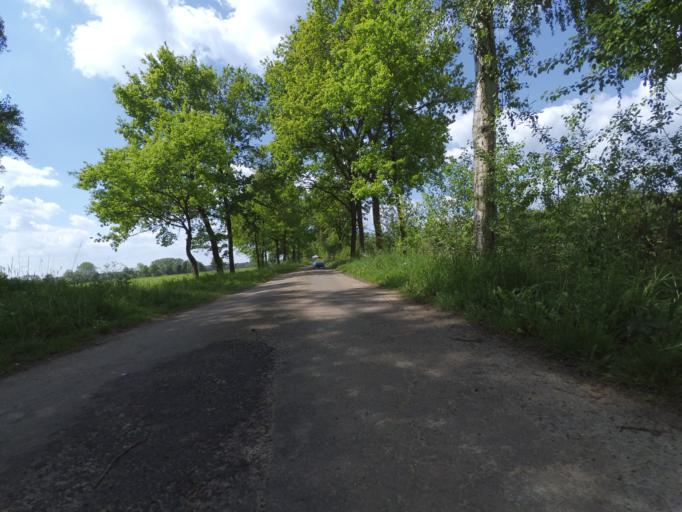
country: DE
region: Lower Saxony
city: Langlingen
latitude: 52.5723
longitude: 10.2421
